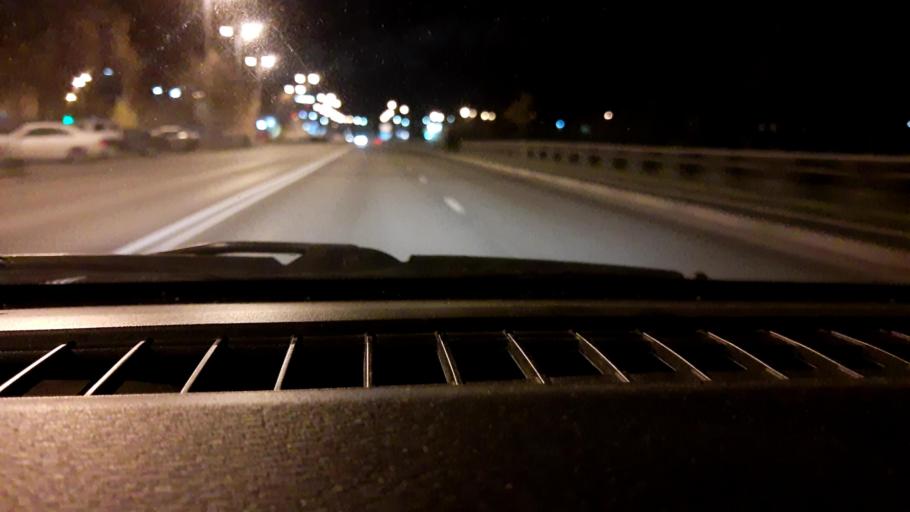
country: RU
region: Nizjnij Novgorod
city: Gorbatovka
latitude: 56.2416
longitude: 43.8558
